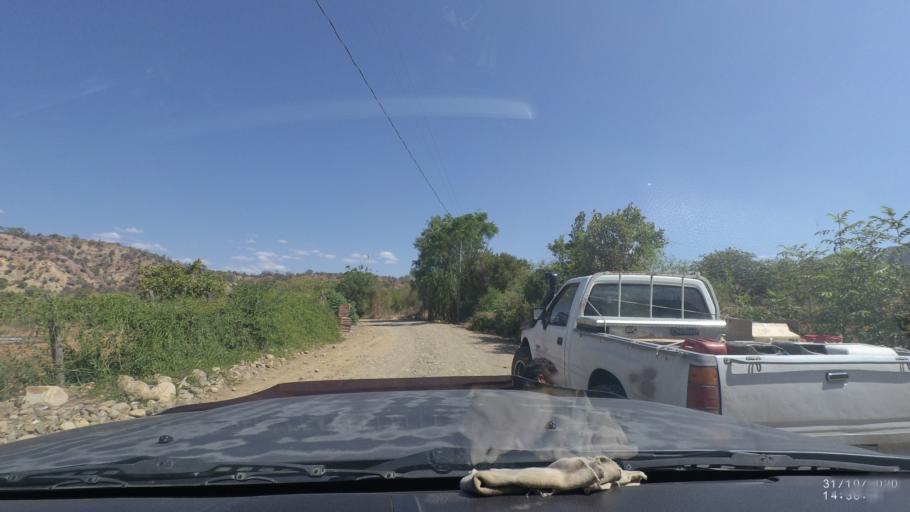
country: BO
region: Cochabamba
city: Aiquile
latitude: -18.1795
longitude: -64.8693
